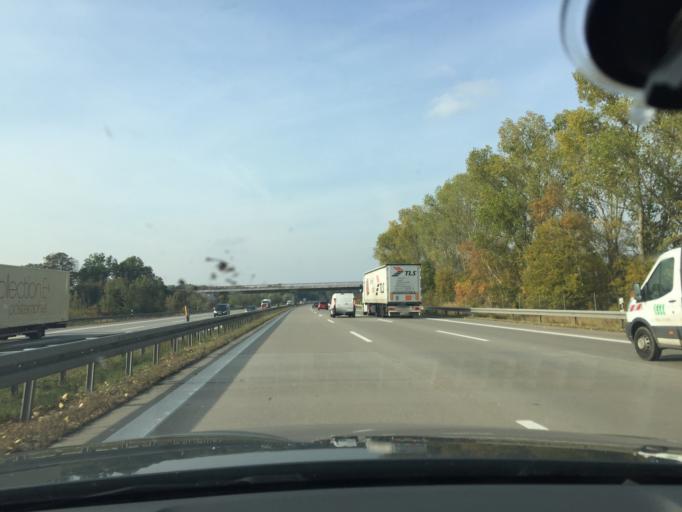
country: DE
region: Brandenburg
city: Neuenhagen
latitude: 52.5618
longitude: 13.6575
